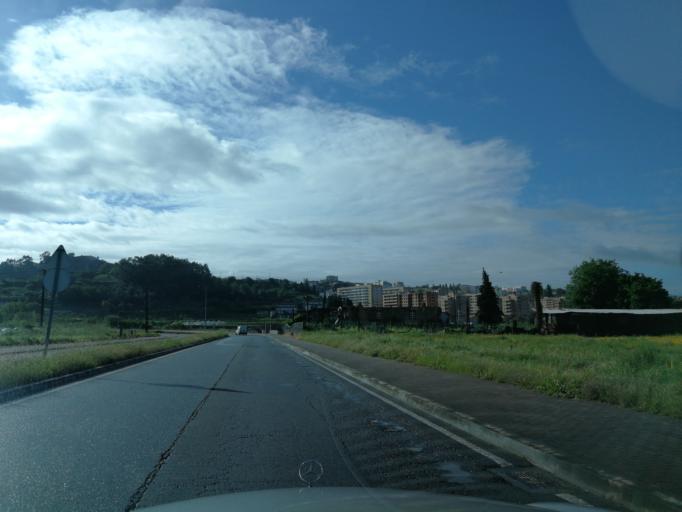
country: PT
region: Braga
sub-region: Braga
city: Braga
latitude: 41.5649
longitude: -8.4387
